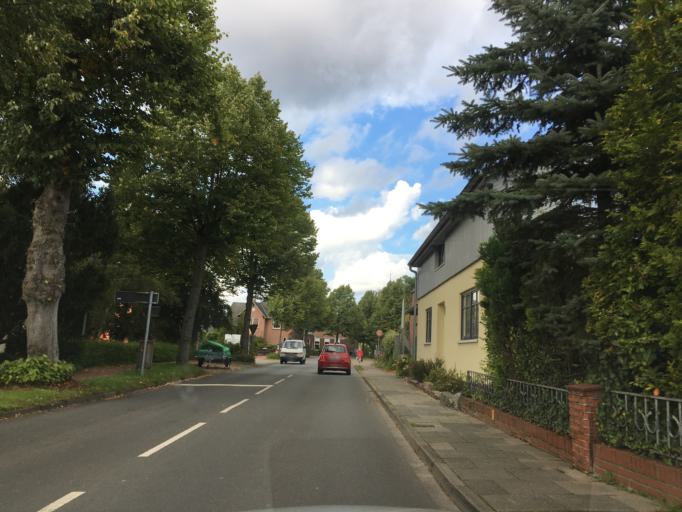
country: DE
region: Schleswig-Holstein
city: Krokau
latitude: 54.3938
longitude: 10.3706
